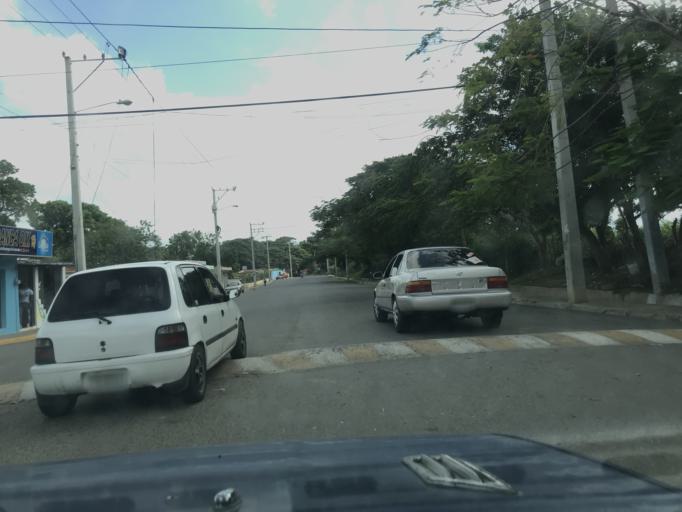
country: DO
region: Santiago
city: Santiago de los Caballeros
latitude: 19.4499
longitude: -70.7301
